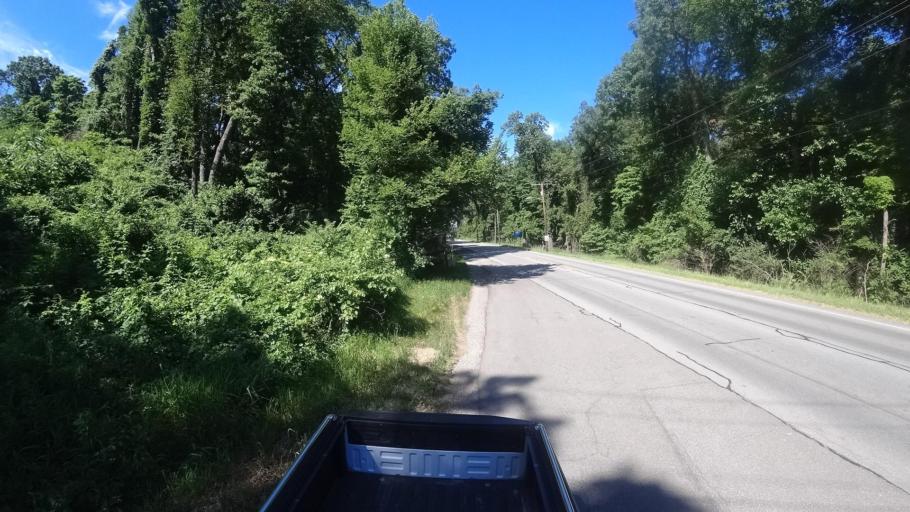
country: US
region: Indiana
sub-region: Porter County
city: Burns Harbor
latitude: 41.6295
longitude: -87.1061
